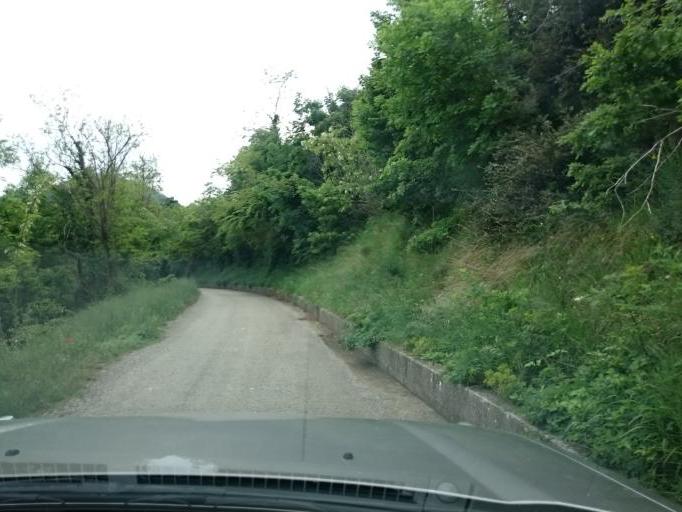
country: IT
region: Veneto
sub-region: Provincia di Padova
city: Baone
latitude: 45.2533
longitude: 11.6736
